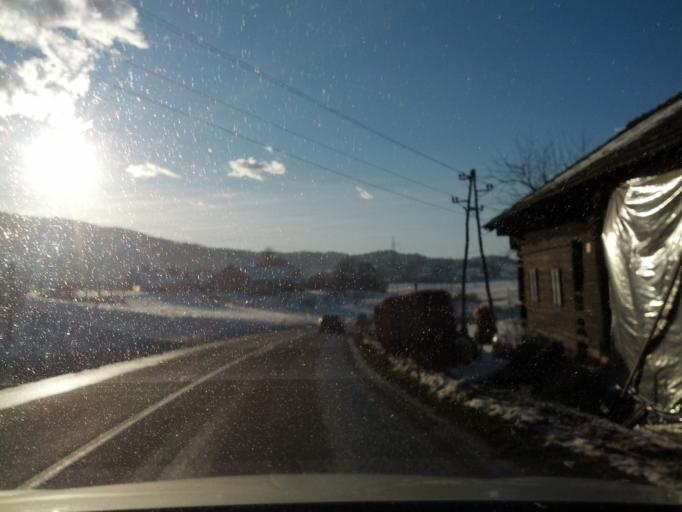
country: SI
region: Moravce
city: Moravce
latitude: 46.1381
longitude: 14.7269
